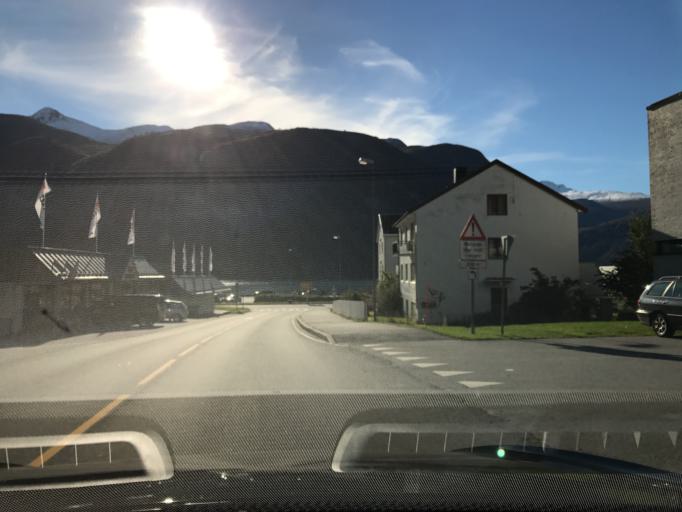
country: NO
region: More og Romsdal
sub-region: Norddal
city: Valldal
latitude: 62.2988
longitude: 7.2623
